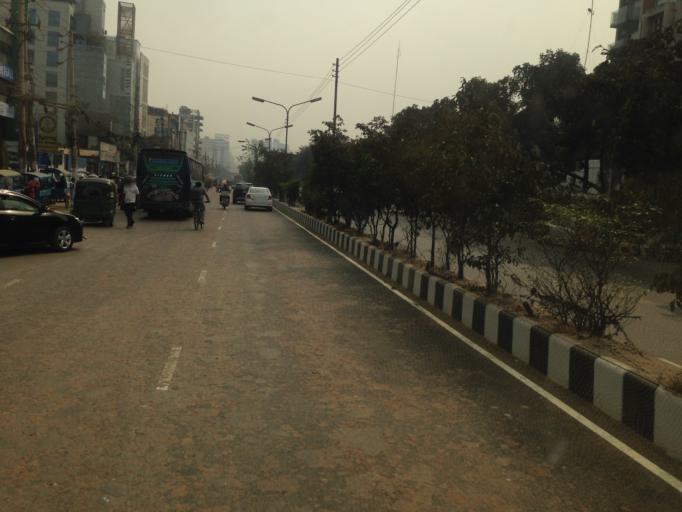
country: BD
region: Dhaka
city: Paltan
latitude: 23.8023
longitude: 90.4227
